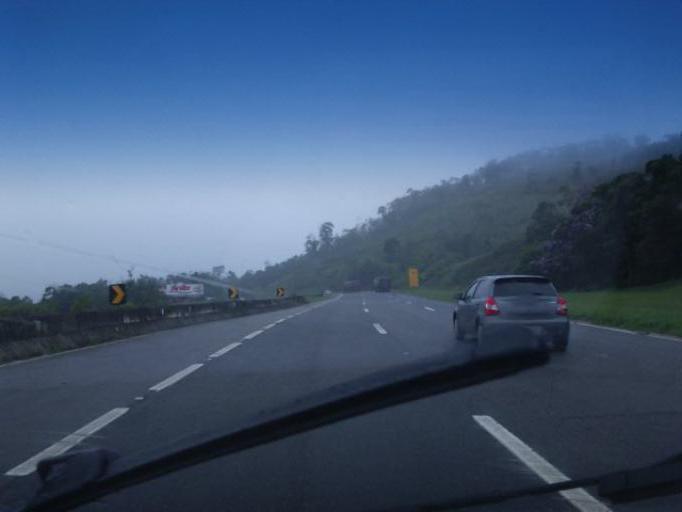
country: BR
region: Parana
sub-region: Campina Grande Do Sul
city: Campina Grande do Sul
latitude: -25.1098
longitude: -48.7994
